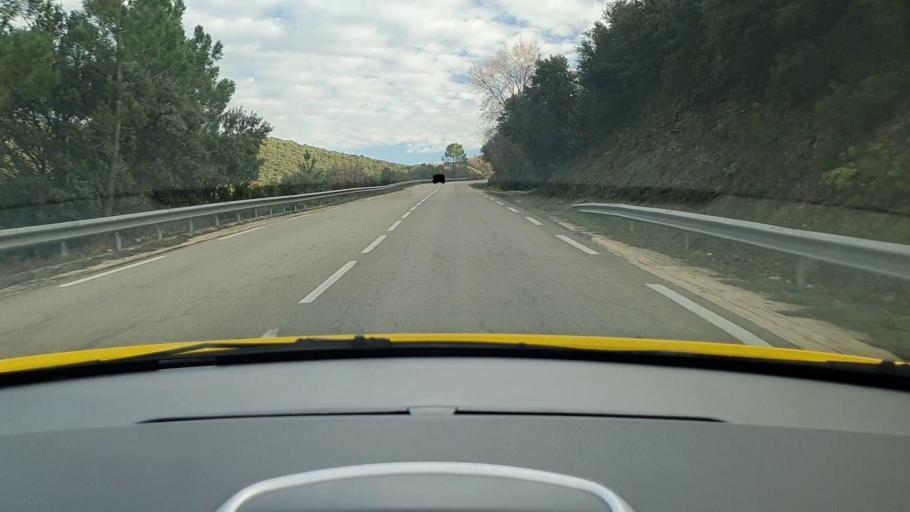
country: FR
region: Languedoc-Roussillon
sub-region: Departement du Gard
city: Laval-Pradel
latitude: 44.2006
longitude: 4.0871
